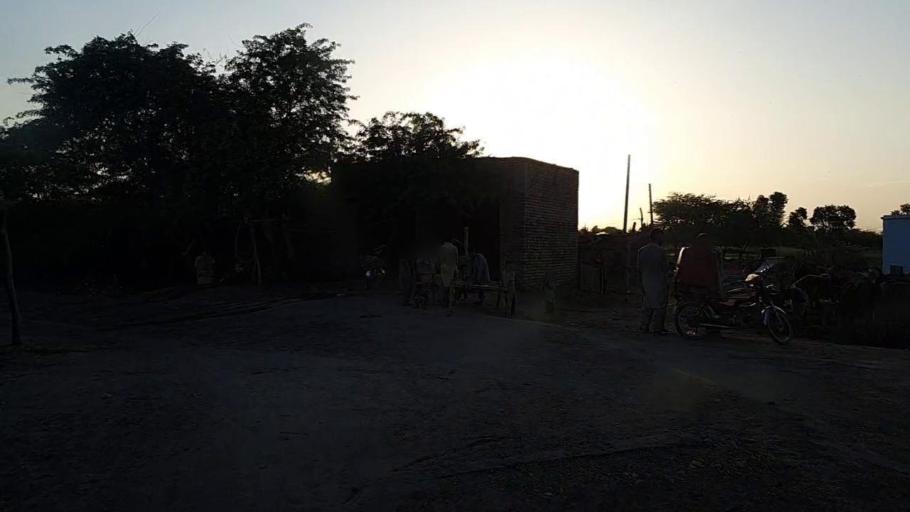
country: PK
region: Sindh
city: Hingorja
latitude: 27.0613
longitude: 68.3942
